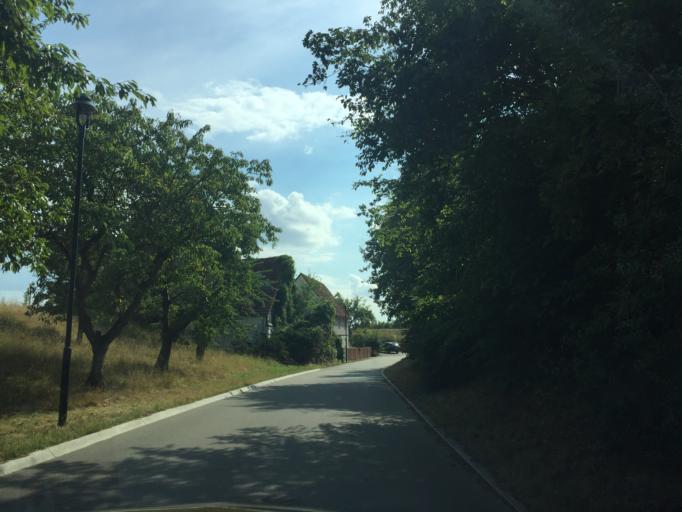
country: DE
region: Thuringia
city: Vollmershain
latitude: 50.8720
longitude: 12.3083
